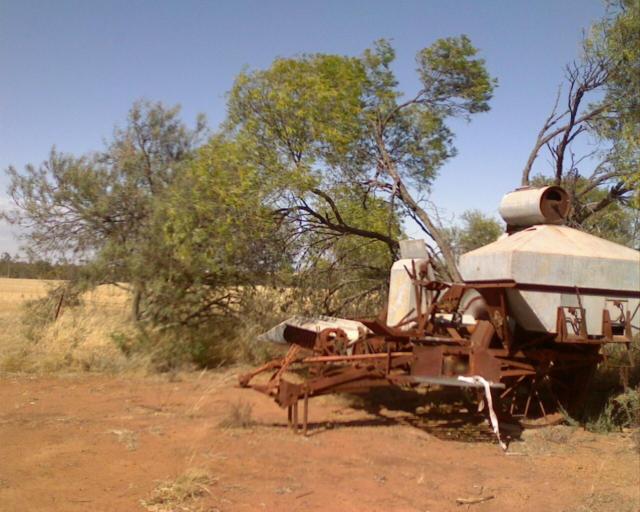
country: AU
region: Western Australia
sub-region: Moora
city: Moora
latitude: -29.8792
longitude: 116.0319
